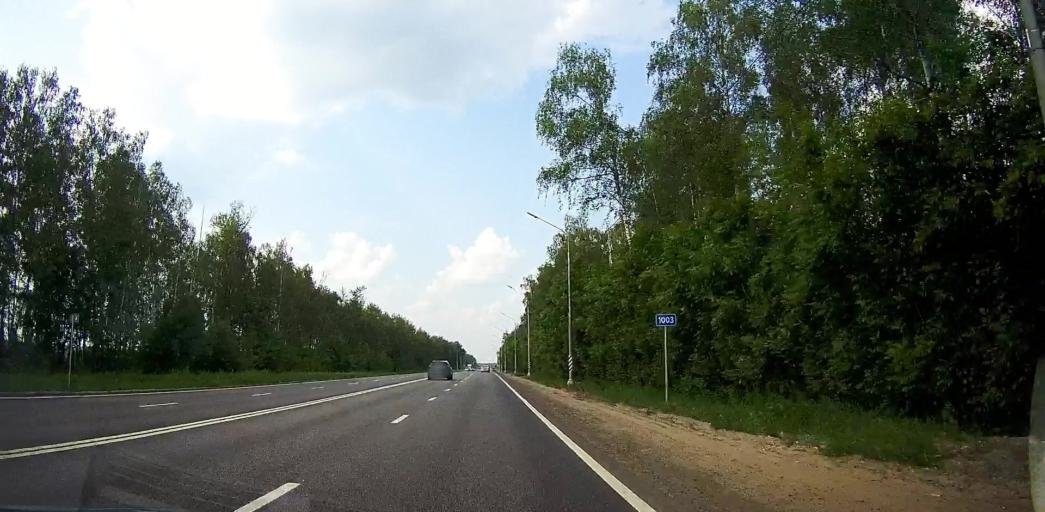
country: RU
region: Moskovskaya
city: Mikhnevo
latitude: 55.1002
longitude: 37.9483
